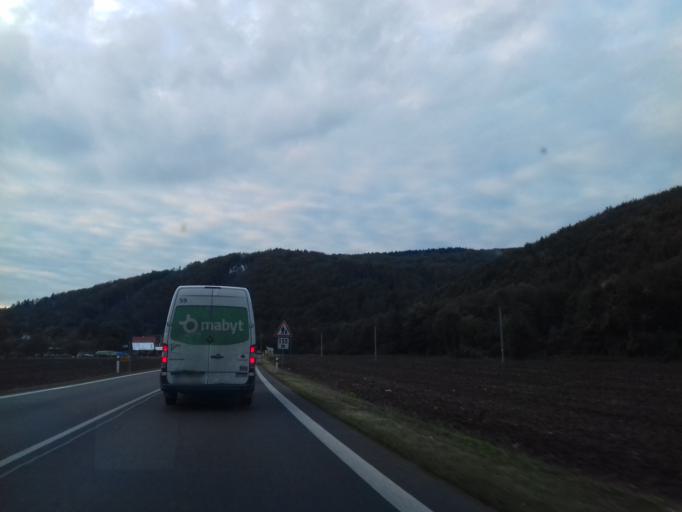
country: SK
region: Trenciansky
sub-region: Okres Trencin
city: Trencin
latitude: 48.9422
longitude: 17.9278
